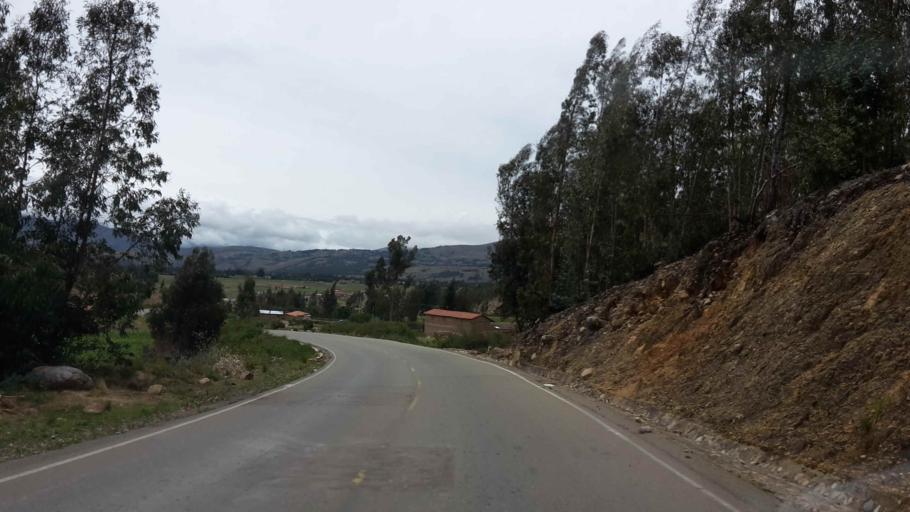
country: BO
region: Cochabamba
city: Arani
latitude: -17.4584
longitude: -65.7091
